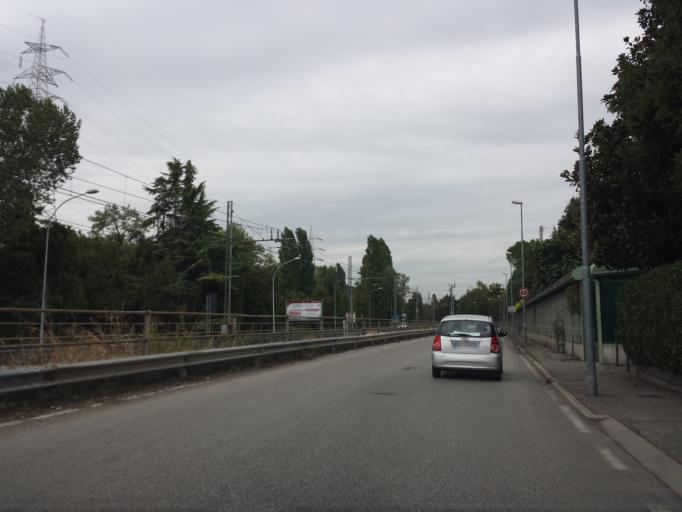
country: IT
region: Veneto
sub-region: Provincia di Padova
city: Padova
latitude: 45.4141
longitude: 11.9147
